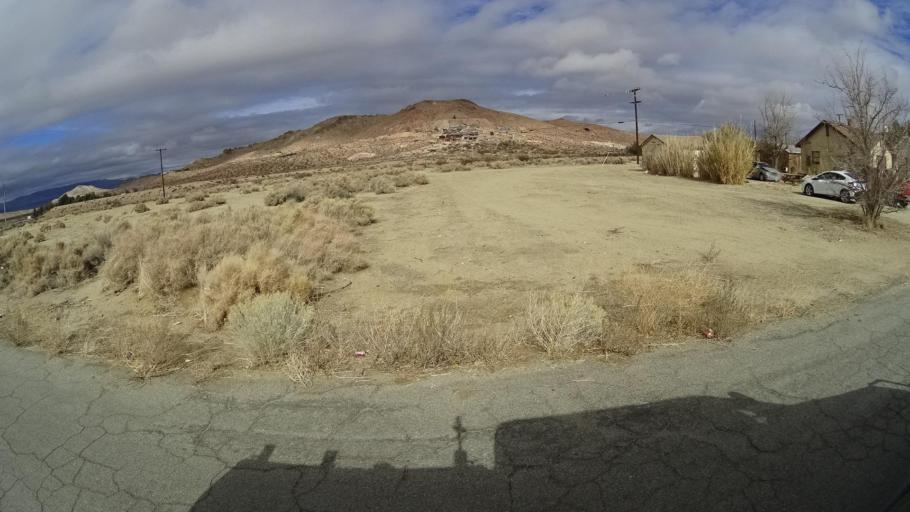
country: US
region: California
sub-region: Kern County
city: Rosamond
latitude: 34.8710
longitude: -118.2322
